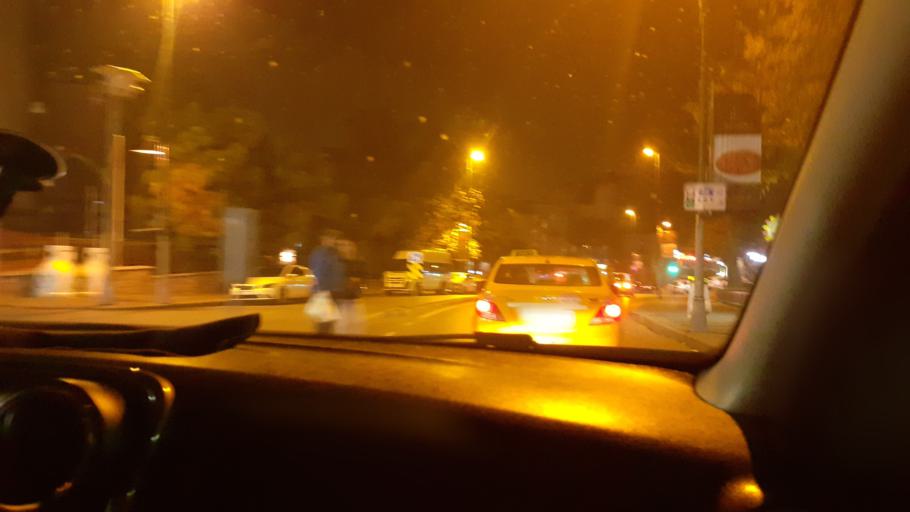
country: TR
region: Istanbul
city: UEskuedar
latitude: 41.0269
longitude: 29.0334
